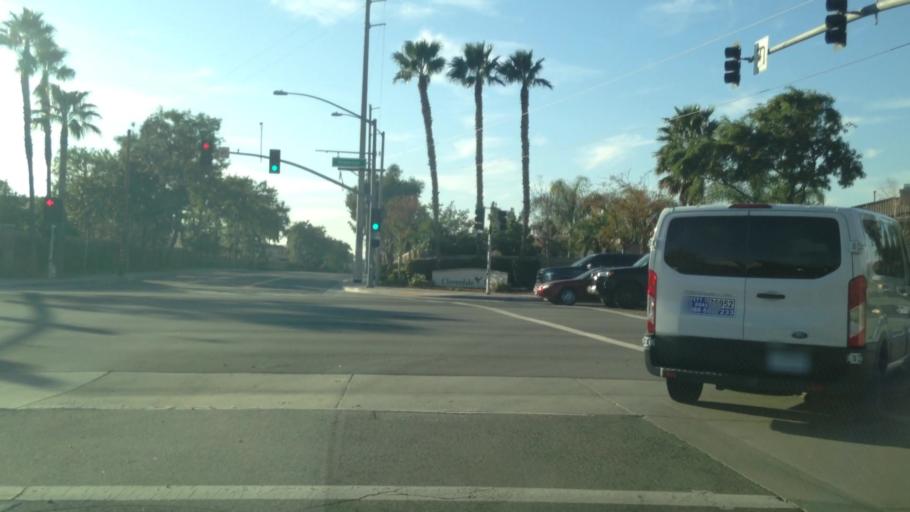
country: US
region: California
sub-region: Riverside County
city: Norco
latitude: 33.9646
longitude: -117.5580
